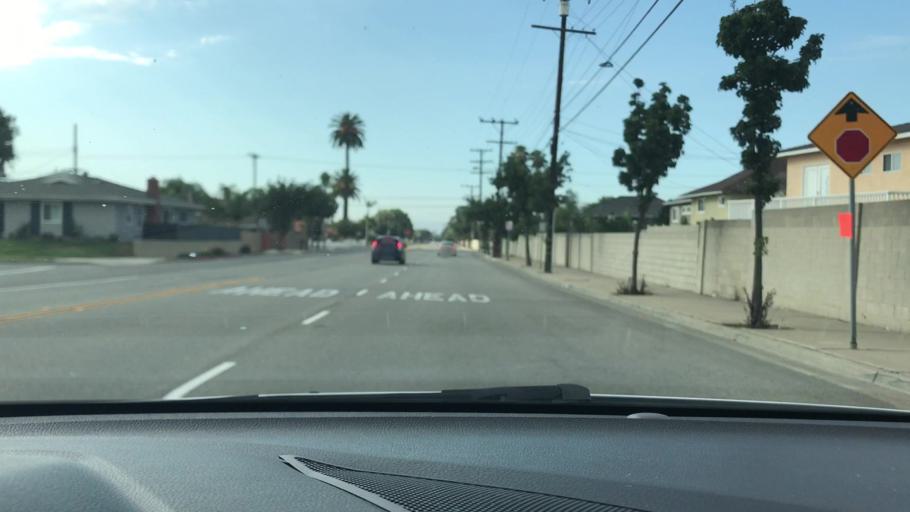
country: US
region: California
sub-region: Orange County
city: North Tustin
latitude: 33.7817
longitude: -117.8184
